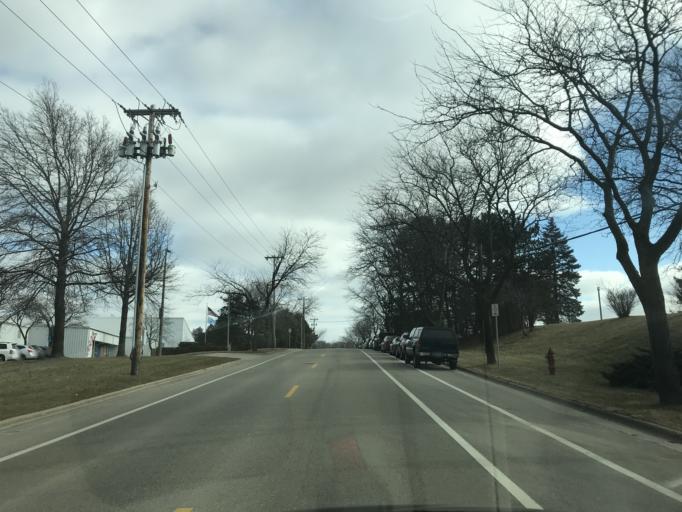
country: US
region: Wisconsin
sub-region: Dane County
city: Monona
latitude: 43.1140
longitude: -89.3039
